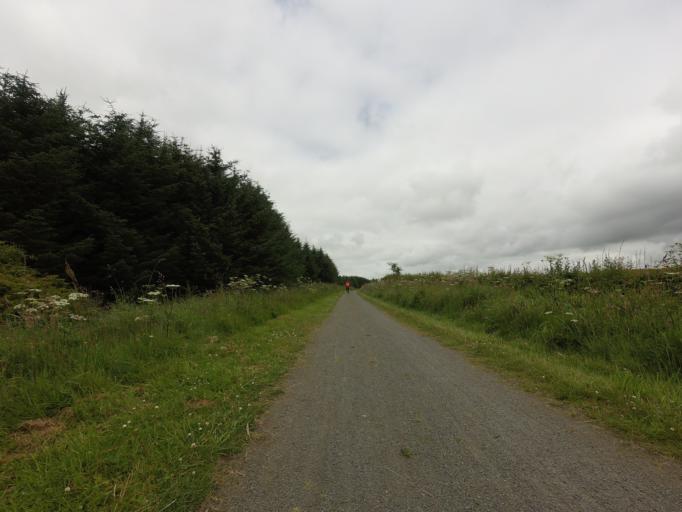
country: GB
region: Scotland
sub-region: Aberdeenshire
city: Mintlaw
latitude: 57.4960
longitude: -2.1393
